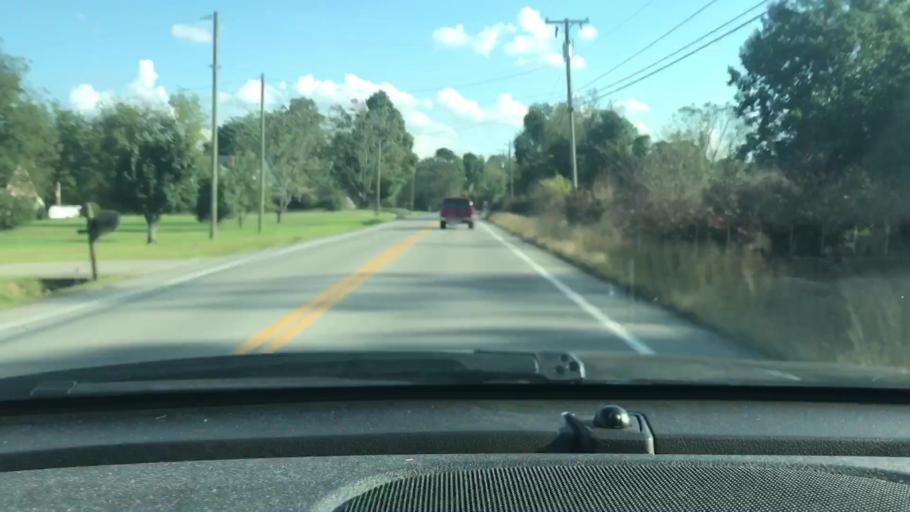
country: US
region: Tennessee
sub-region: Sumner County
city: Shackle Island
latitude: 36.3792
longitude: -86.6192
